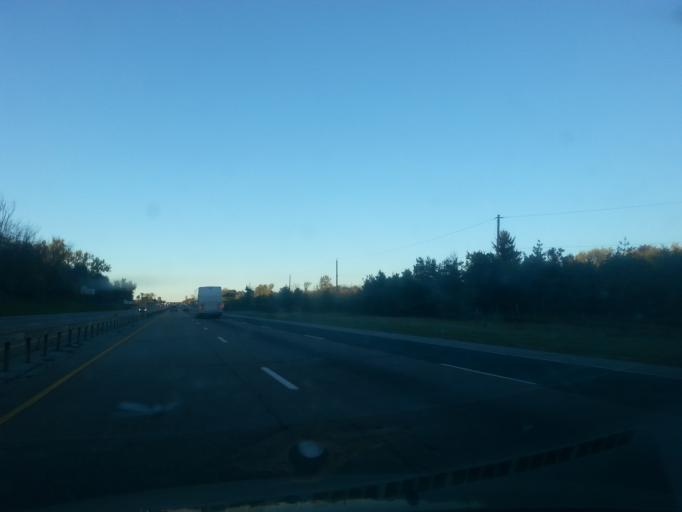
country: CA
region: Ontario
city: Innisfil
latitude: 44.2212
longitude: -79.6625
